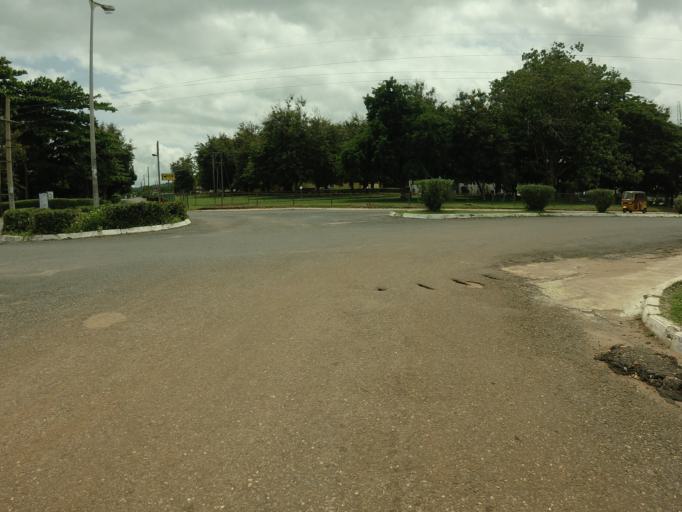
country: GH
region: Volta
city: Ho
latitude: 6.5906
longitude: 0.4691
